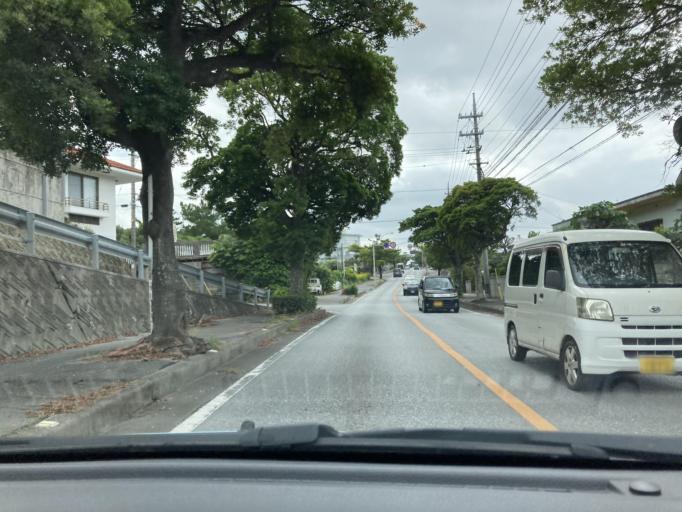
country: JP
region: Okinawa
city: Ginowan
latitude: 26.2693
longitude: 127.7777
